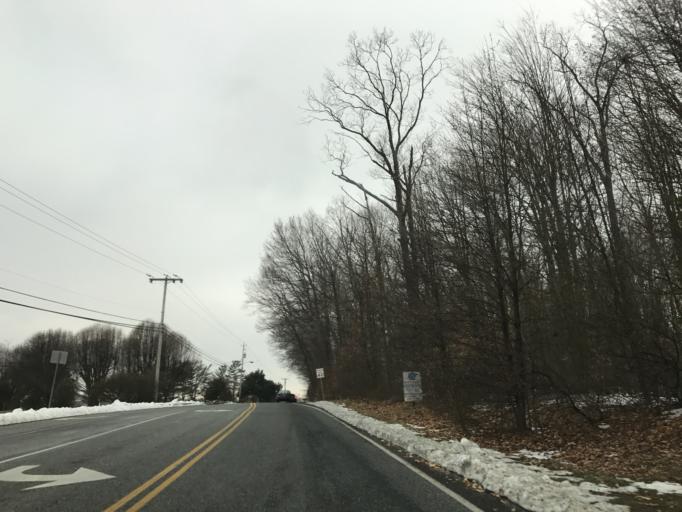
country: US
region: Maryland
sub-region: Harford County
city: Bel Air South
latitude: 39.5245
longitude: -76.2866
